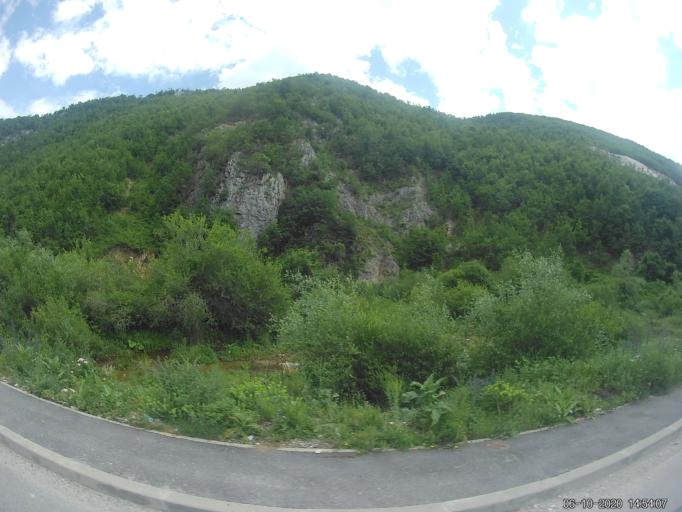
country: XK
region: Ferizaj
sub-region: Komuna e Shtimes
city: Shtime
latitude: 42.4047
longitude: 20.9909
